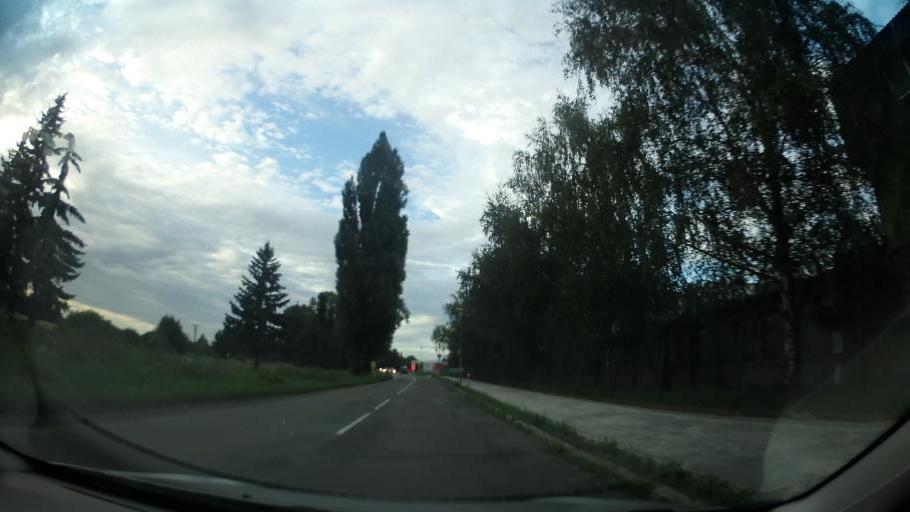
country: CZ
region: Olomoucky
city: Cervenka
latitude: 49.7146
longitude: 17.0763
